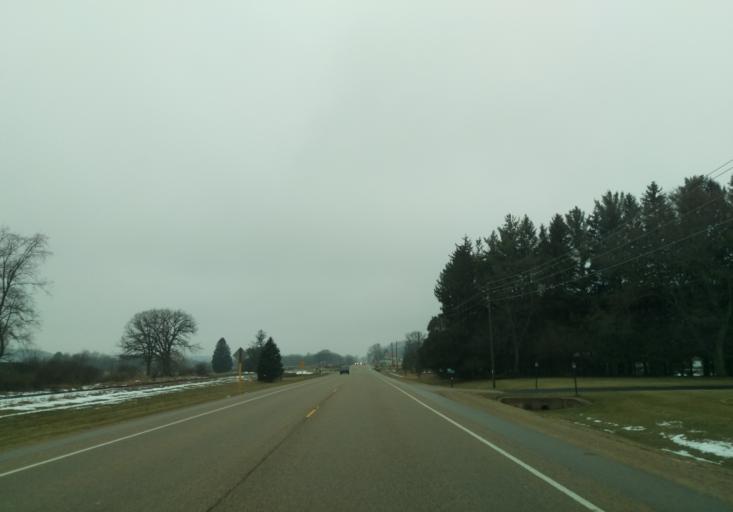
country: US
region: Wisconsin
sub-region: Dane County
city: Cross Plains
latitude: 43.1156
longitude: -89.6669
